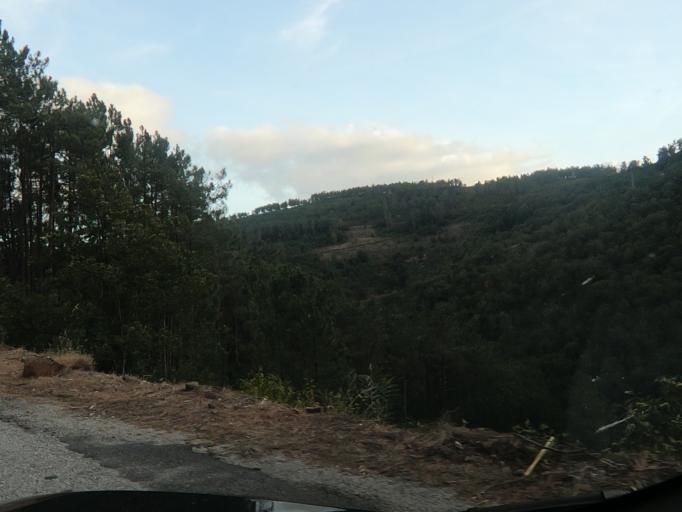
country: PT
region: Vila Real
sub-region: Santa Marta de Penaguiao
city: Santa Marta de Penaguiao
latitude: 41.2446
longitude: -7.8494
